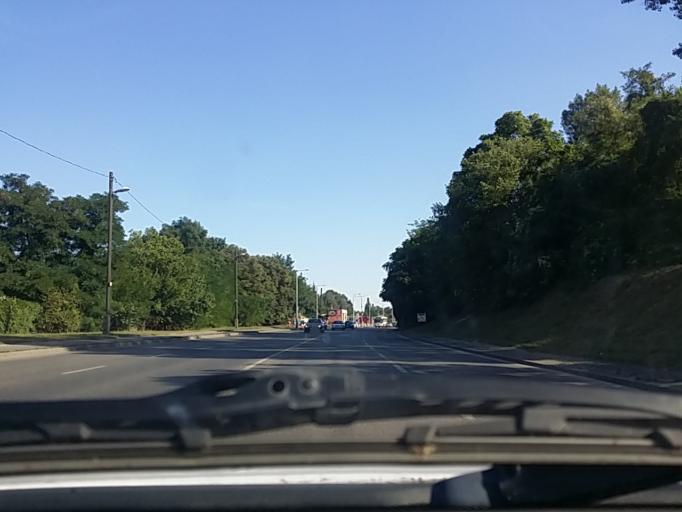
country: HU
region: Pest
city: Urom
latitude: 47.5672
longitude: 19.0211
